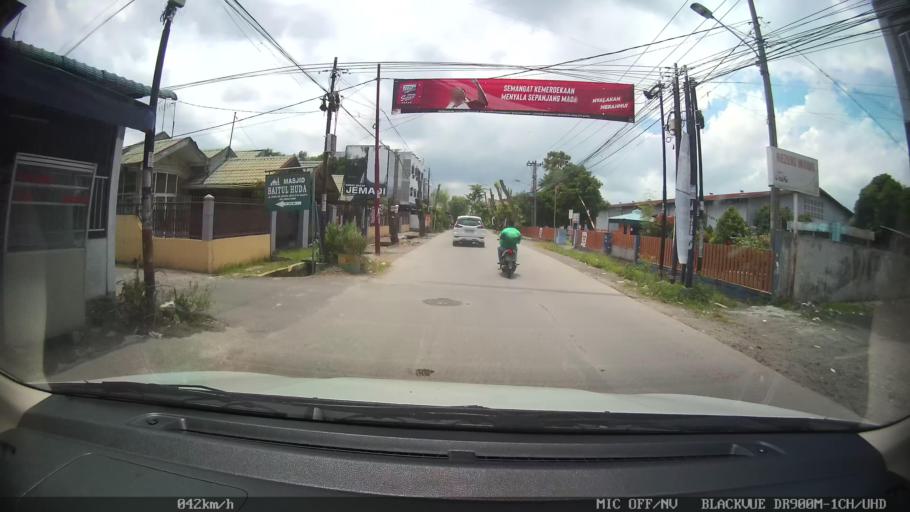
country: ID
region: North Sumatra
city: Medan
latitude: 3.6261
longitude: 98.6789
